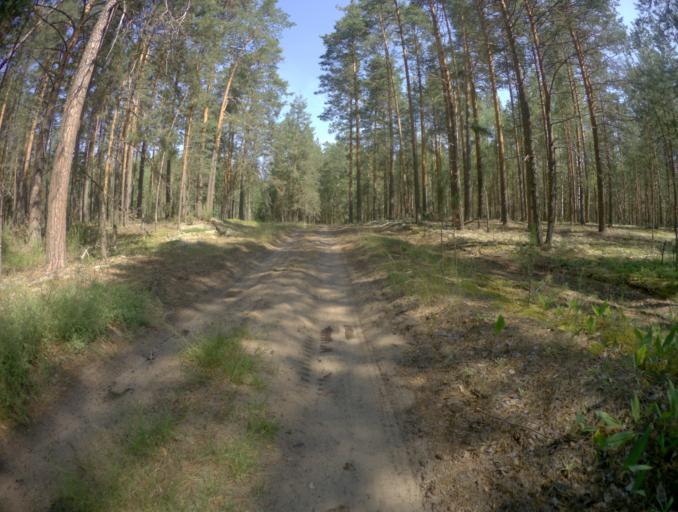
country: RU
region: Ivanovo
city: Talitsy
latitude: 56.3924
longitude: 42.2575
